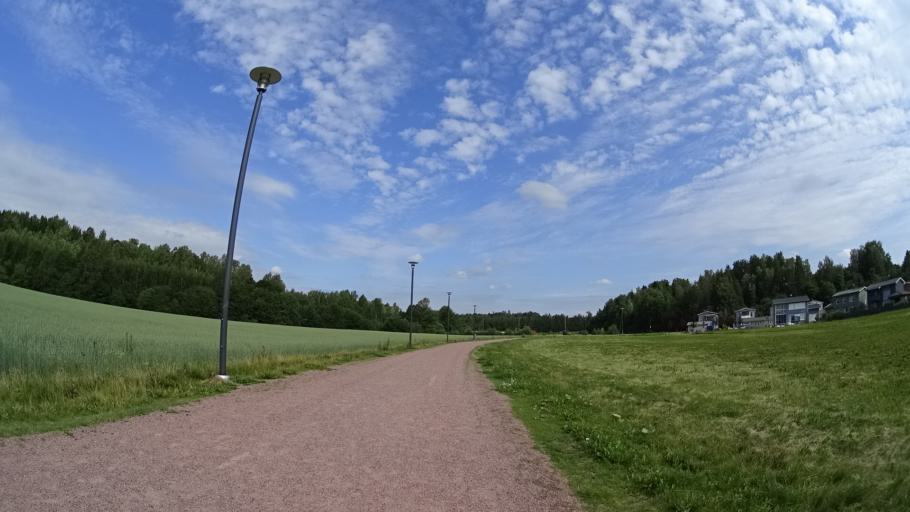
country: FI
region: Uusimaa
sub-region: Helsinki
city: Espoo
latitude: 60.1925
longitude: 24.5857
